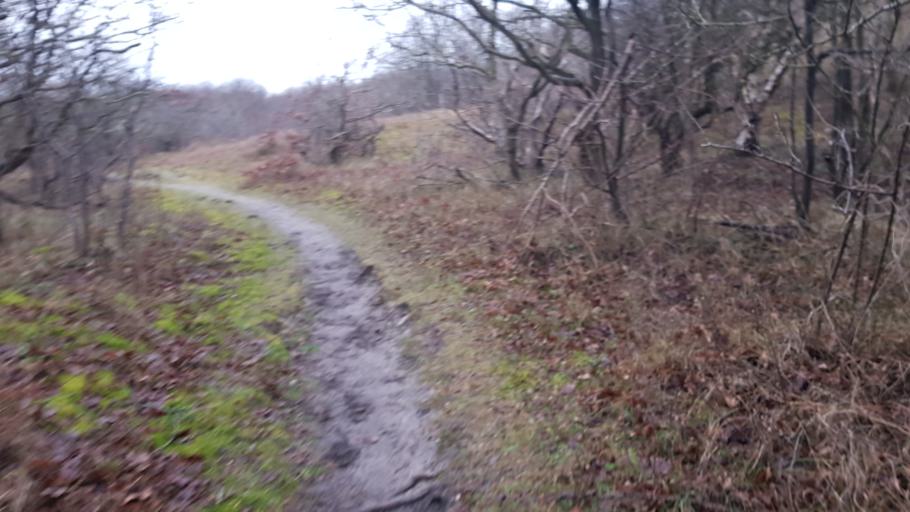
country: NL
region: North Holland
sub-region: Gemeente Bergen
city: Egmond aan Zee
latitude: 52.6527
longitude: 4.6381
